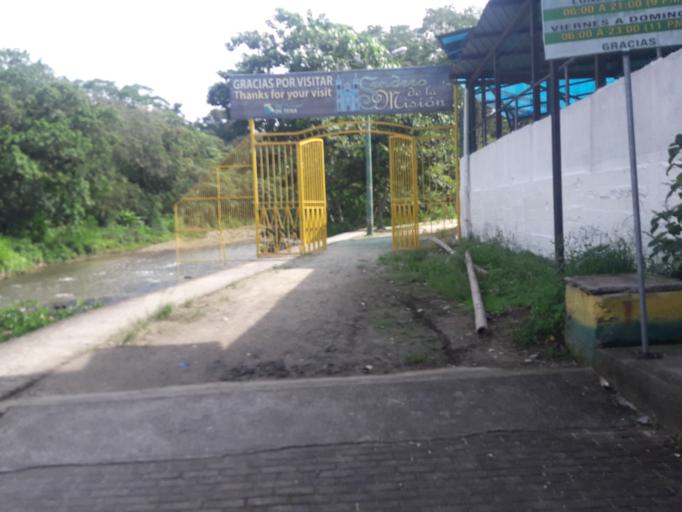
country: EC
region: Napo
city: Tena
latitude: -0.9929
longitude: -77.8161
